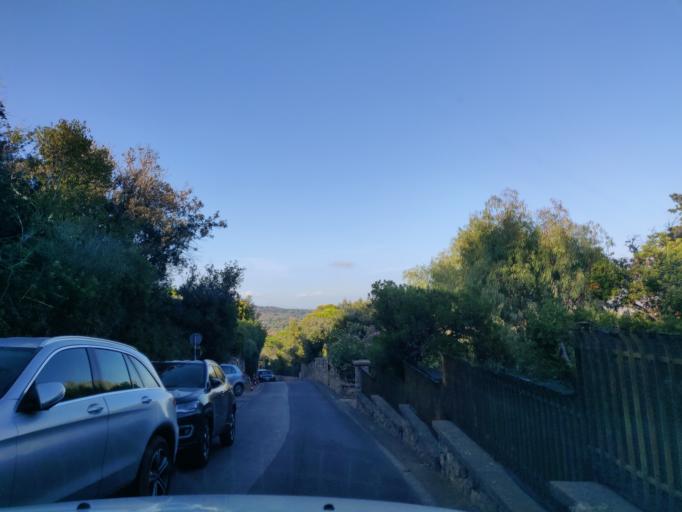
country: IT
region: Tuscany
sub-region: Provincia di Grosseto
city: Orbetello Scalo
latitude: 42.4075
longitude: 11.2903
